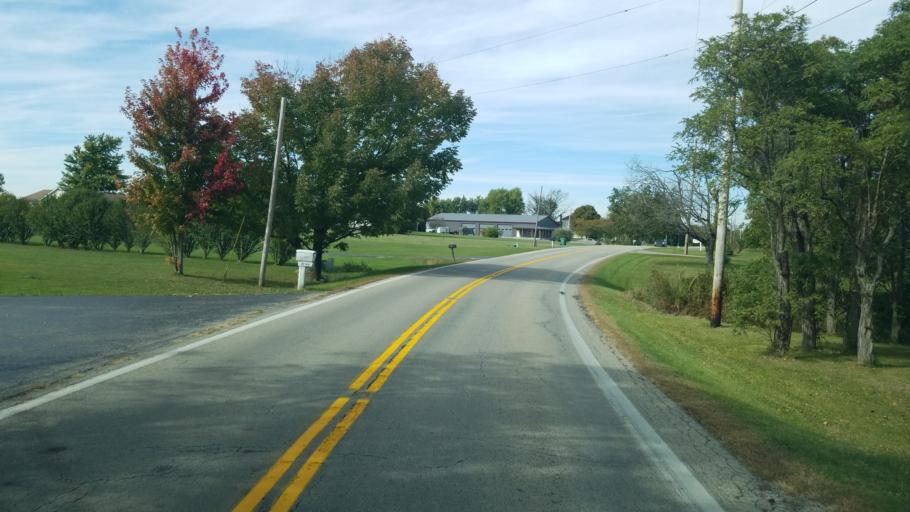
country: US
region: Ohio
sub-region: Highland County
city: Leesburg
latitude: 39.3282
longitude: -83.5904
